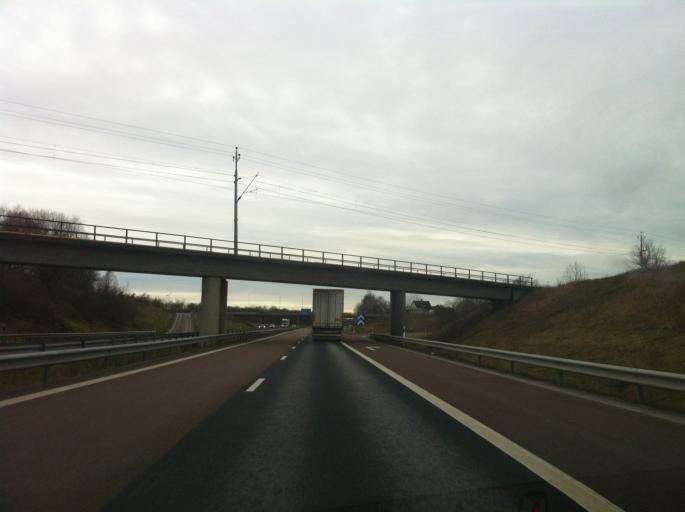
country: SE
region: Skane
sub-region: Astorps Kommun
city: Astorp
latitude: 56.1411
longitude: 12.9612
